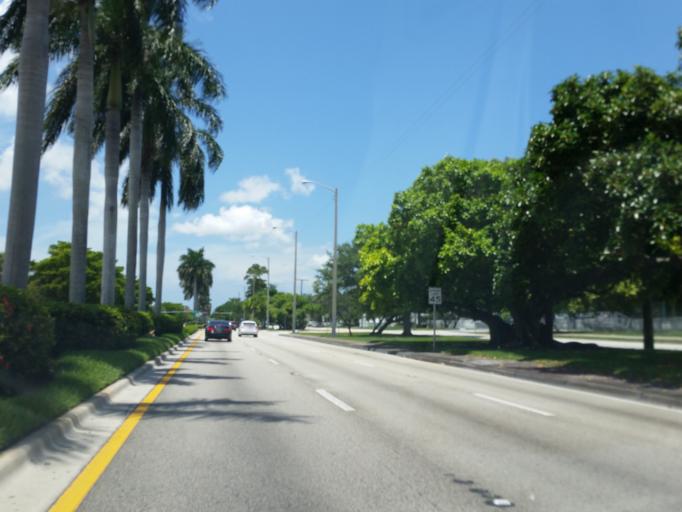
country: US
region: Florida
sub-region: Miami-Dade County
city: Coral Gables
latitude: 25.7176
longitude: -80.2731
